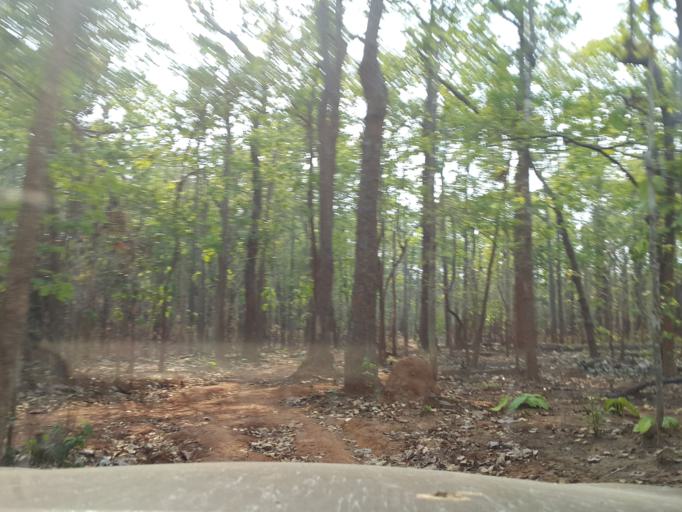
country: TH
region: Lamphun
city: Li
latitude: 17.6085
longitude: 98.9281
